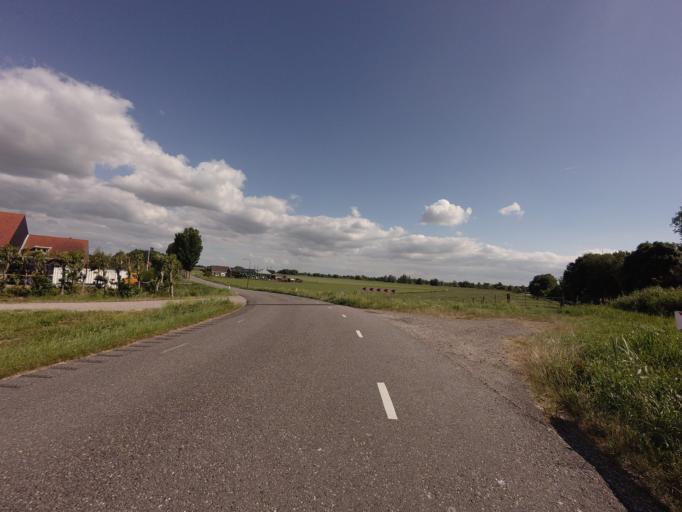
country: NL
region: North Holland
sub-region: Gemeente Uithoorn
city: Uithoorn
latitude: 52.2074
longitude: 4.8189
